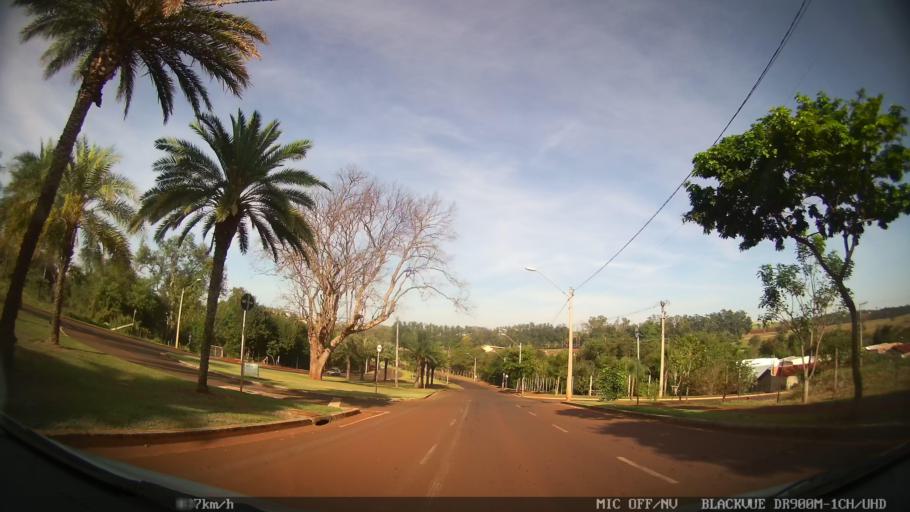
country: BR
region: Sao Paulo
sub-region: Ribeirao Preto
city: Ribeirao Preto
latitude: -21.2580
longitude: -47.8197
